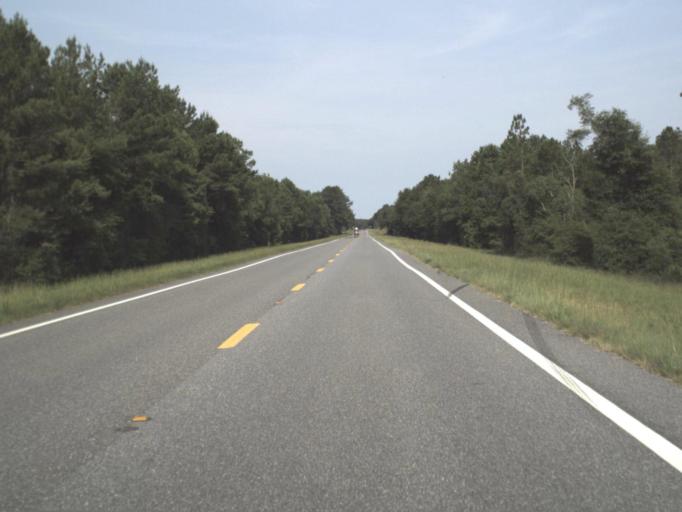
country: US
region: Florida
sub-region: Suwannee County
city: Wellborn
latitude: 30.3201
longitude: -82.7848
